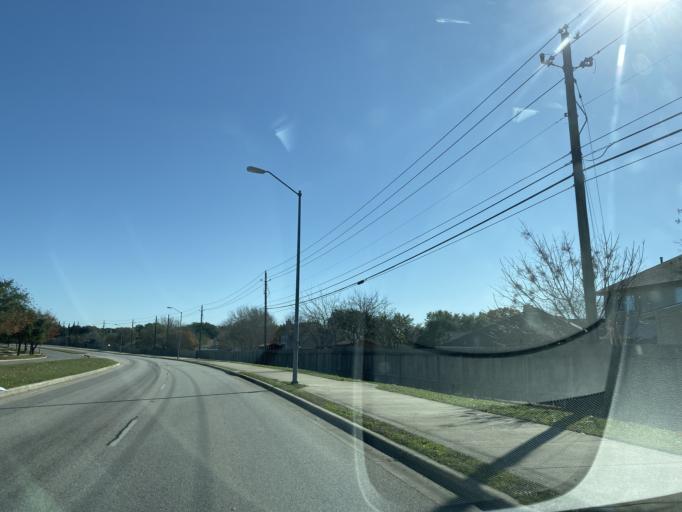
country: US
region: Texas
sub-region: Travis County
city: Windemere
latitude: 30.4717
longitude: -97.6523
